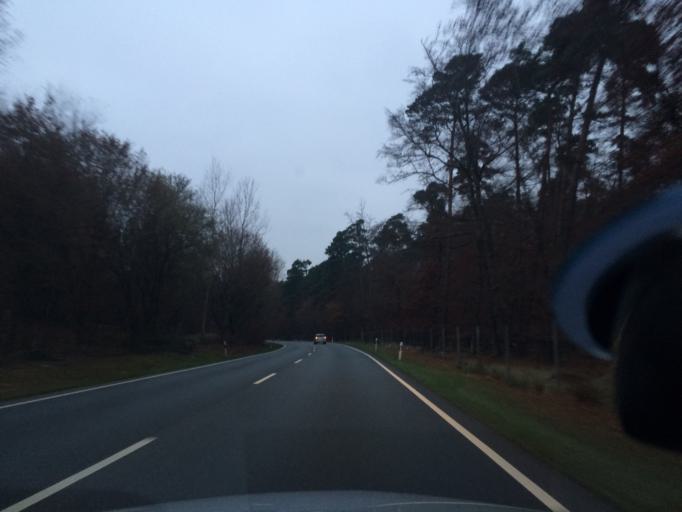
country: DE
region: Hesse
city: Raunheim
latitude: 49.9862
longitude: 8.4796
